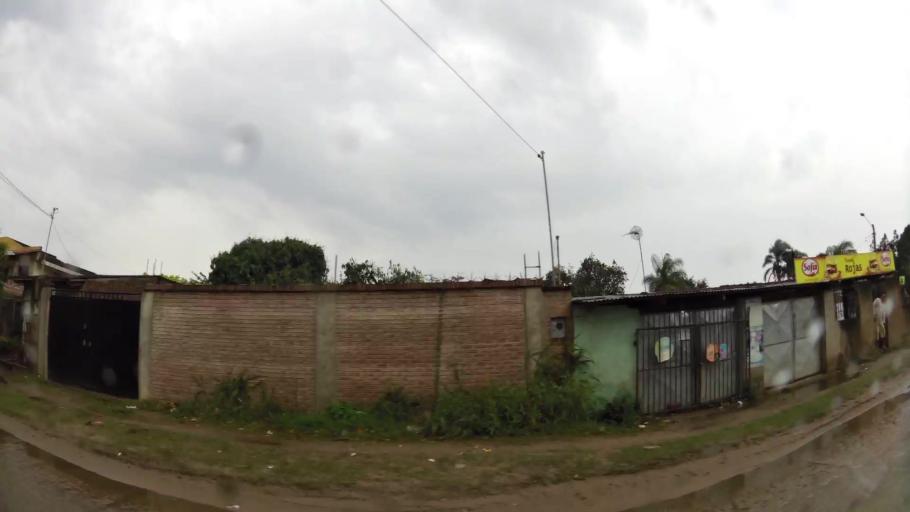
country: BO
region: Santa Cruz
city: Santa Cruz de la Sierra
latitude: -17.7612
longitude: -63.1150
